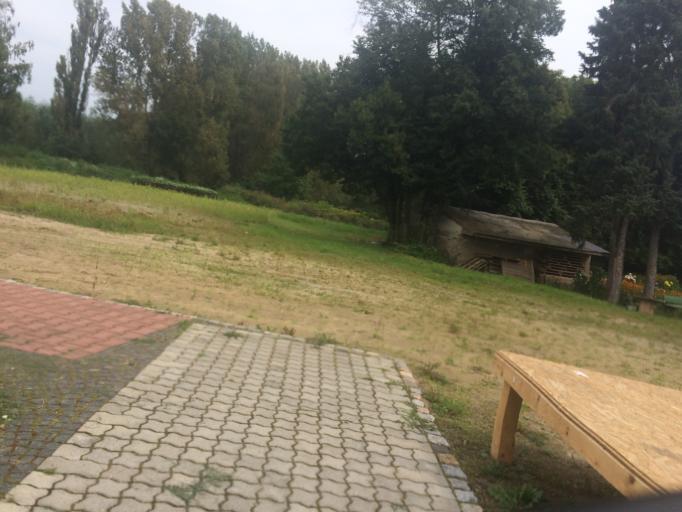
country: DE
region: Berlin
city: Heinersdorf
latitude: 52.5695
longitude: 13.4464
